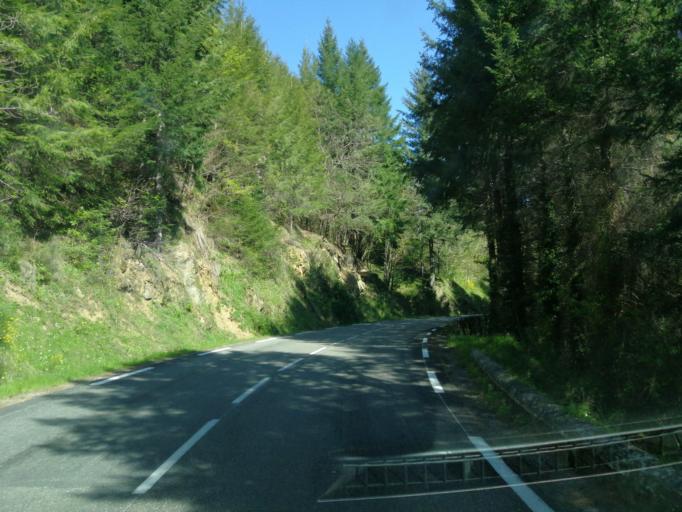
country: FR
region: Rhone-Alpes
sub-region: Departement de l'Ardeche
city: Le Cheylard
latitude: 44.8966
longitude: 4.4855
